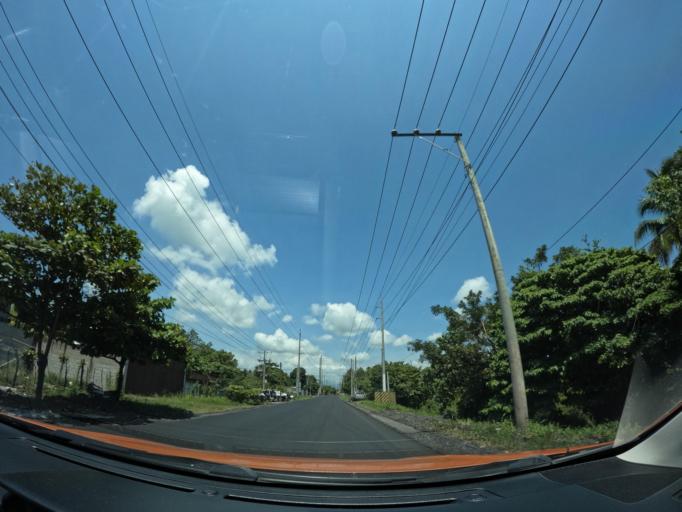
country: GT
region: Escuintla
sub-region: Municipio de Masagua
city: Masagua
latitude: 14.2047
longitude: -90.8426
